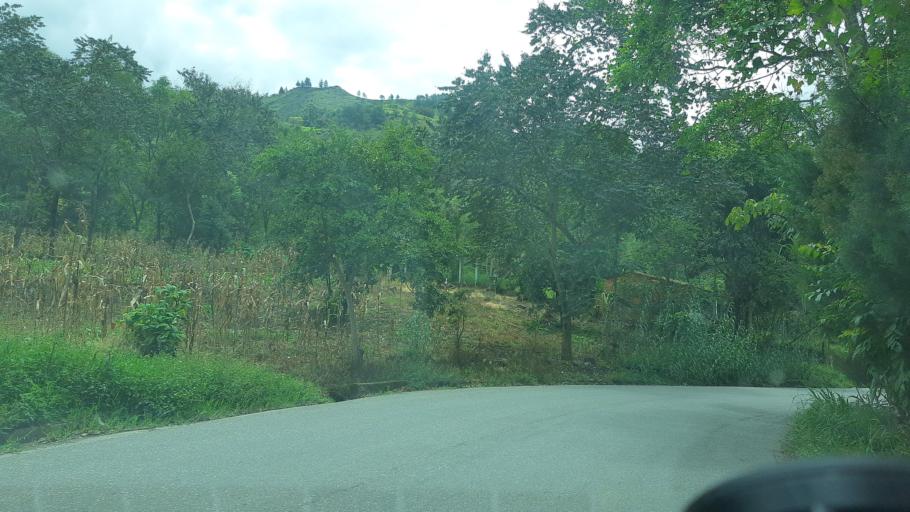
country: CO
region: Cundinamarca
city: Tenza
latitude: 5.0358
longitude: -73.3893
